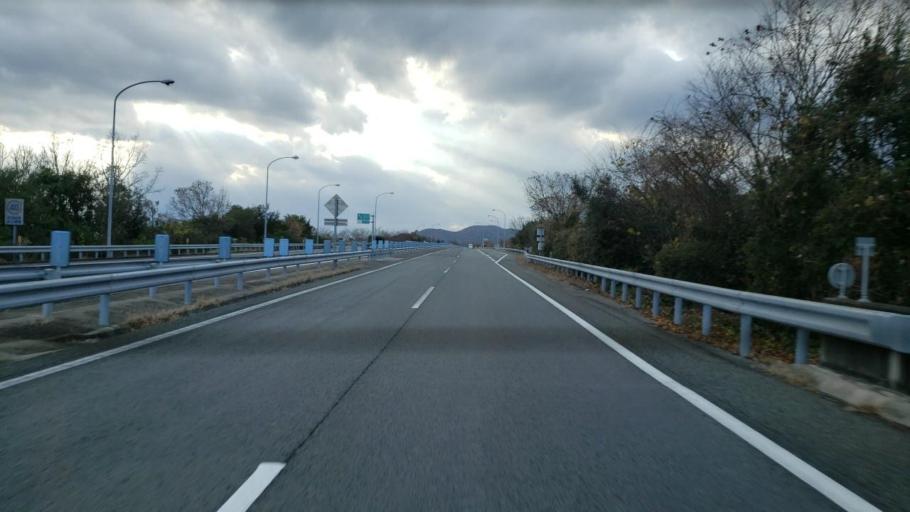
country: JP
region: Tokushima
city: Kamojimacho-jogejima
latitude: 34.1219
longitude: 134.3585
